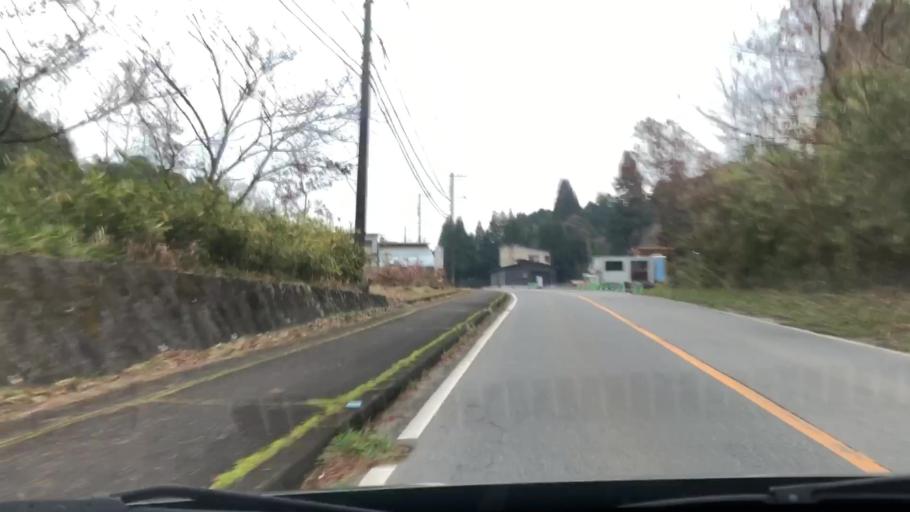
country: JP
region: Oita
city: Usuki
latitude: 33.0050
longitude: 131.6510
